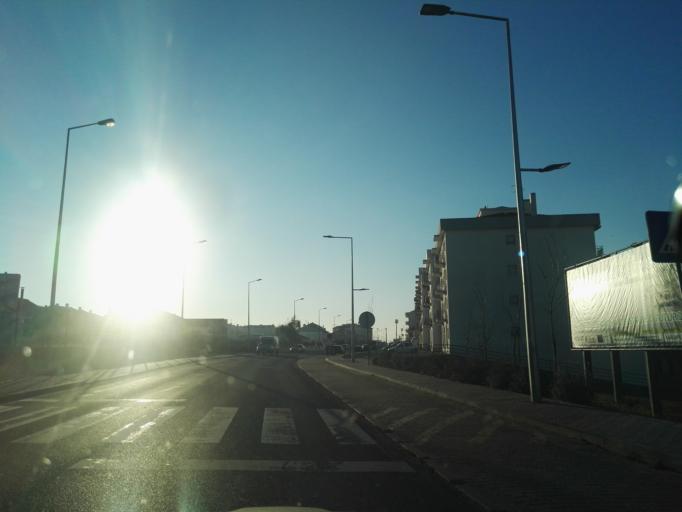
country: PT
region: Santarem
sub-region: Benavente
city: Samora Correia
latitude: 38.9252
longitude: -8.8833
